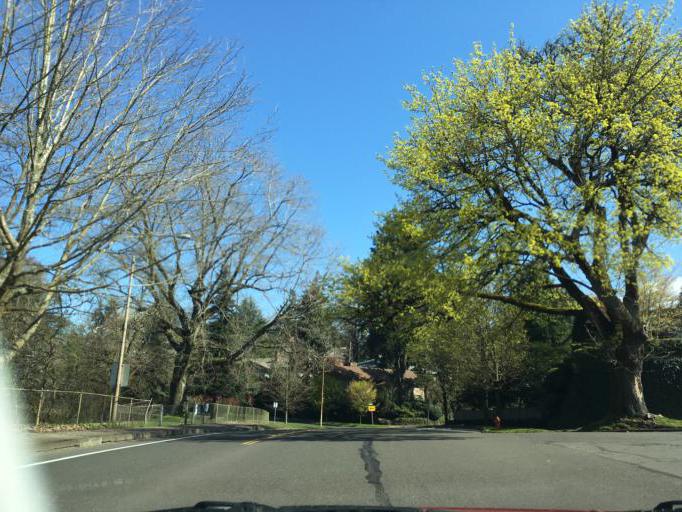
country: US
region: Oregon
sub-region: Clackamas County
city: Milwaukie
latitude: 45.4770
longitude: -122.6346
